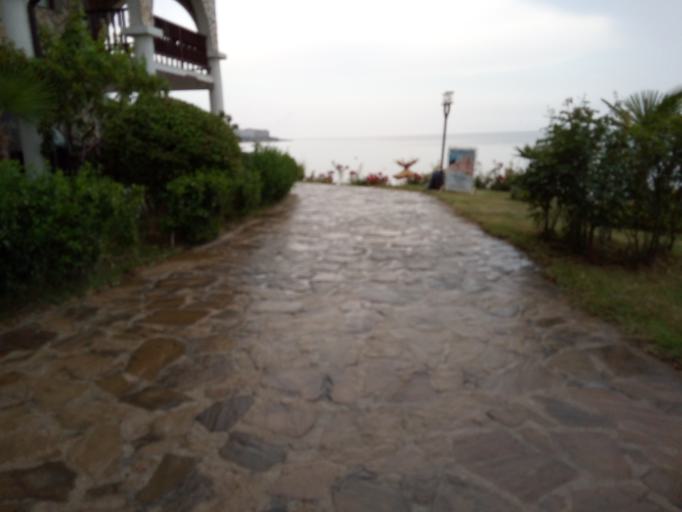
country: BG
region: Burgas
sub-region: Obshtina Nesebur
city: Sveti Vlas
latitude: 42.7055
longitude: 27.7763
